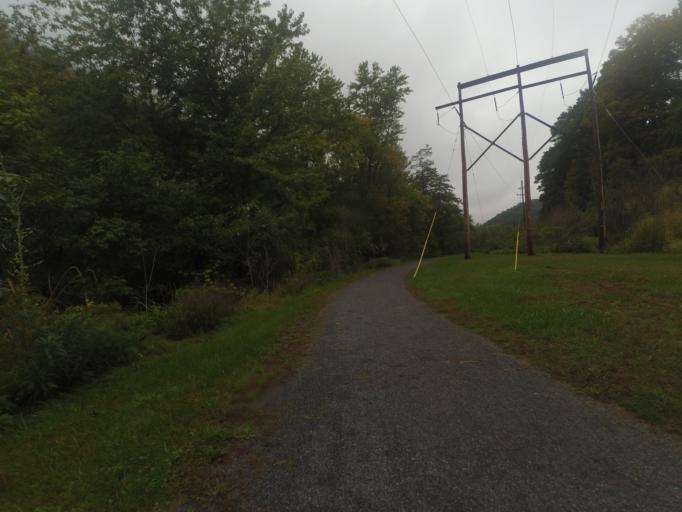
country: US
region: Pennsylvania
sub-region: Huntingdon County
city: McConnellstown
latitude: 40.5674
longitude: -78.1267
